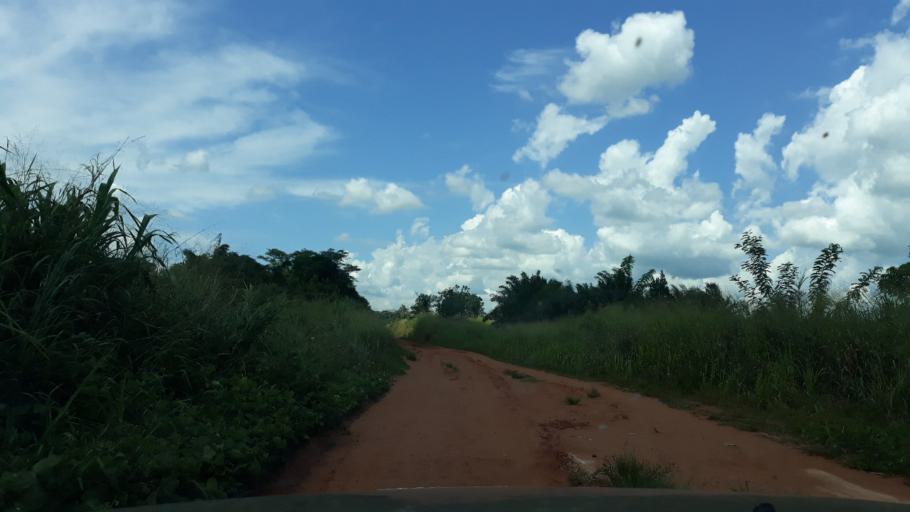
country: CD
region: Equateur
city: Businga
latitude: 3.4042
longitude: 20.3866
